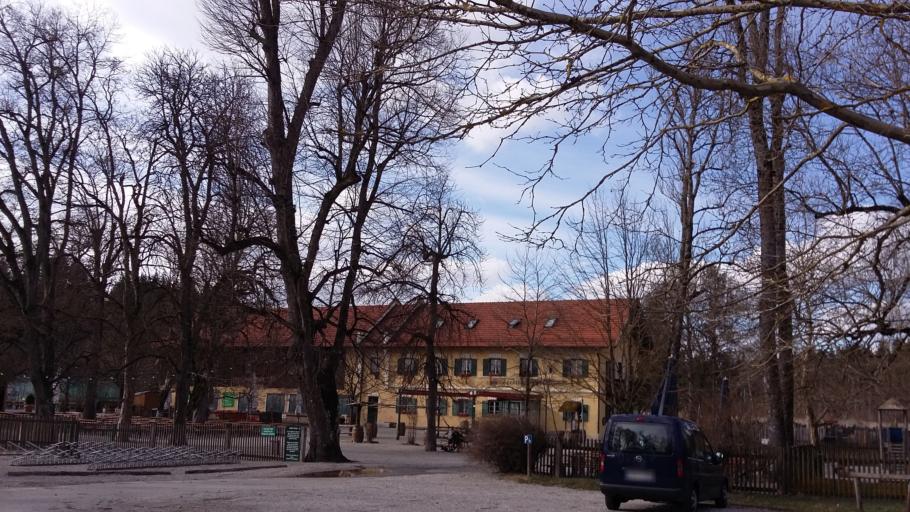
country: DE
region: Bavaria
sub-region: Upper Bavaria
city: Planegg
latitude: 48.0752
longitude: 11.4180
